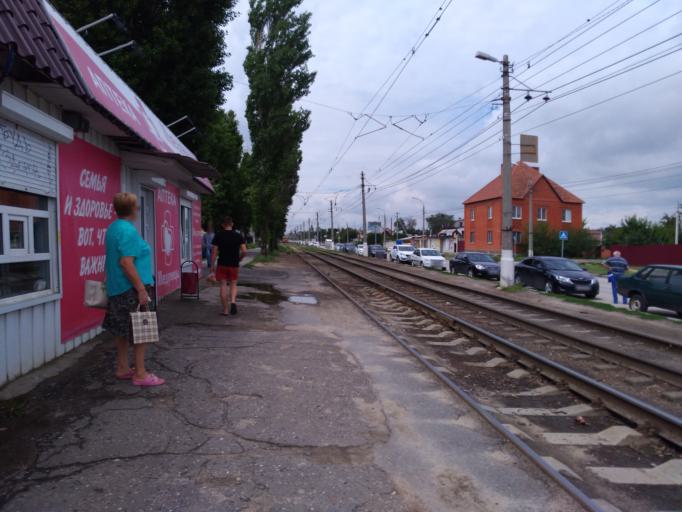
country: RU
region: Volgograd
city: Volgograd
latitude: 48.7155
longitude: 44.4903
